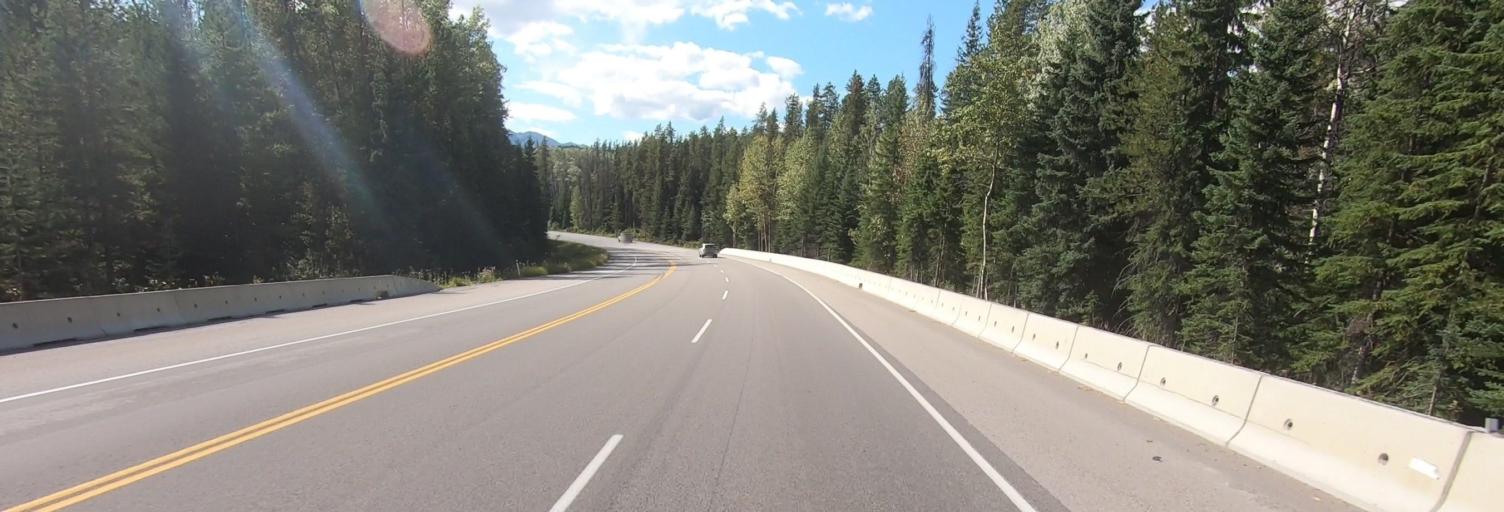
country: CA
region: British Columbia
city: Golden
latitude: 51.2226
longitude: -116.6081
